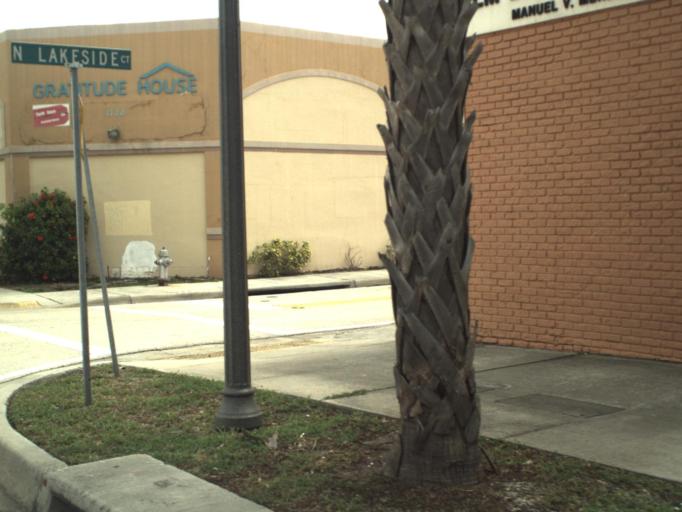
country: US
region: Florida
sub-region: Palm Beach County
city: West Palm Beach
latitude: 26.7282
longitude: -80.0531
